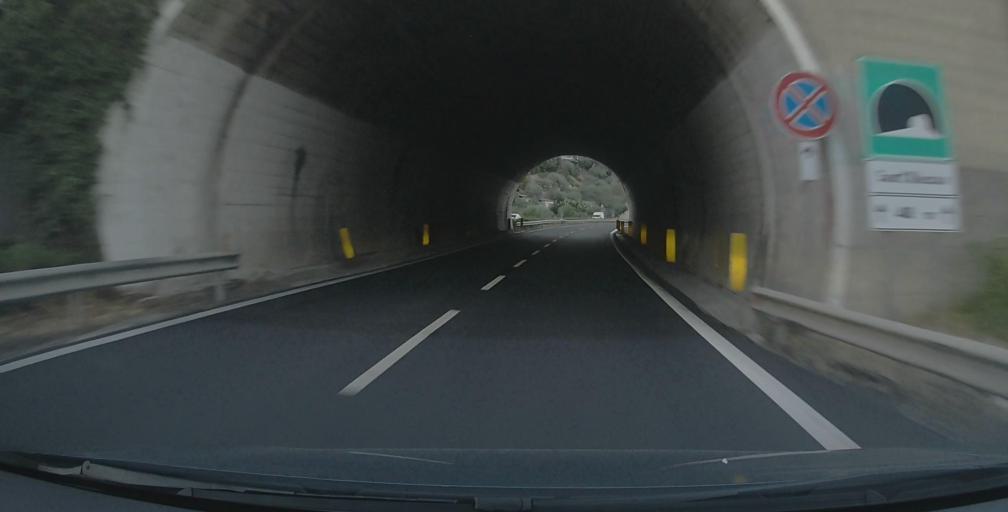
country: IT
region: Sicily
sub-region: Messina
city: Sant'Alessio Siculo
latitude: 37.9225
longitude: 15.3445
